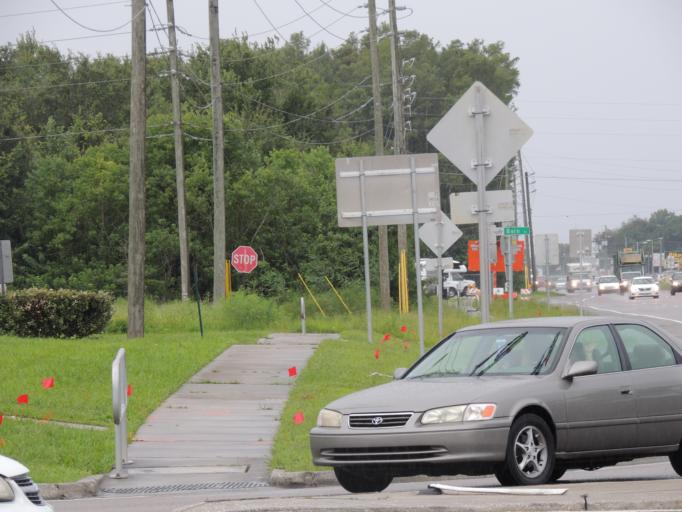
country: US
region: Florida
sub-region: Orange County
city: Hunters Creek
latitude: 28.3391
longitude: -81.4044
